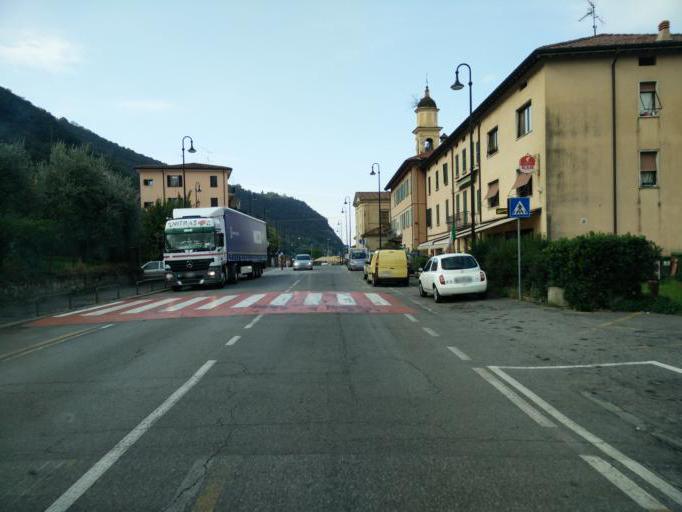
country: IT
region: Lombardy
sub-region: Provincia di Brescia
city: Sulzano
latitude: 45.6746
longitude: 10.0804
